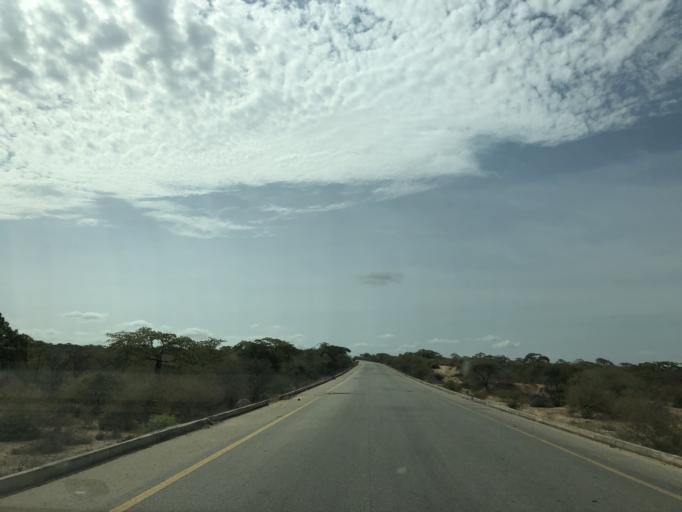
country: AO
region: Benguela
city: Benguela
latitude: -13.0144
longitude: 13.7180
